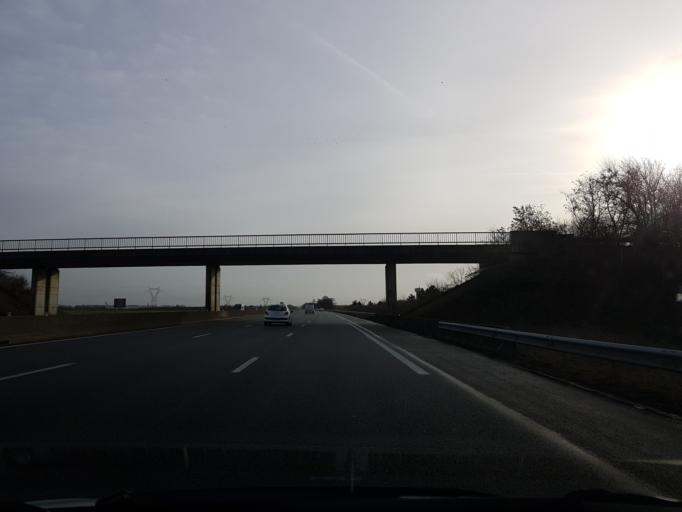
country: FR
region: Ile-de-France
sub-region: Departement de Seine-et-Marne
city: Moissy-Cramayel
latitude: 48.6054
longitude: 2.5873
